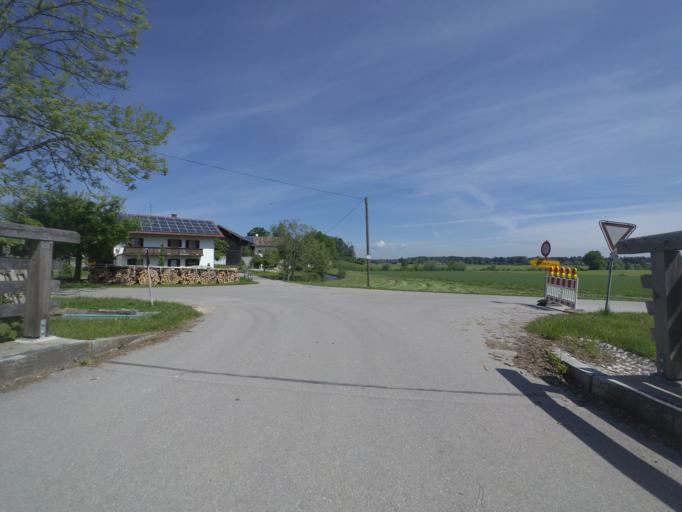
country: DE
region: Bavaria
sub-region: Upper Bavaria
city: Petting
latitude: 47.8889
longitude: 12.8279
